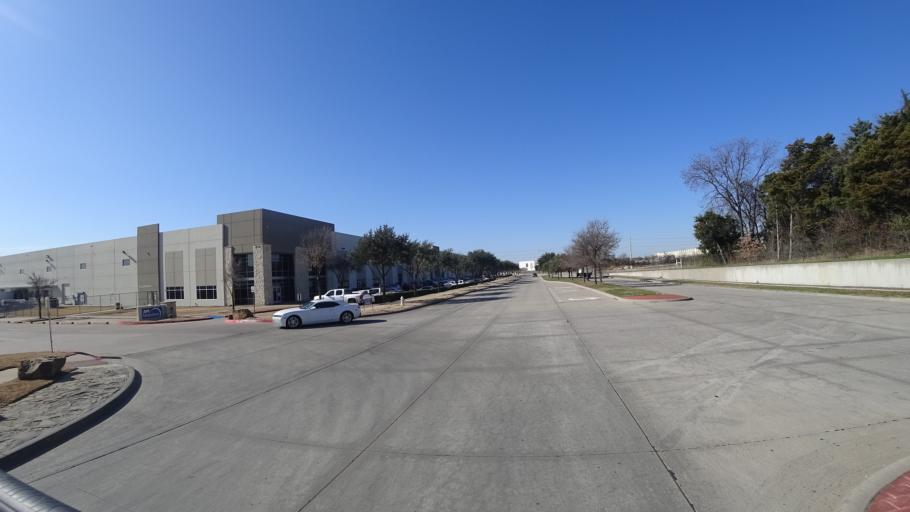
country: US
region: Texas
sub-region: Dallas County
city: Coppell
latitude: 32.9985
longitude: -97.0081
